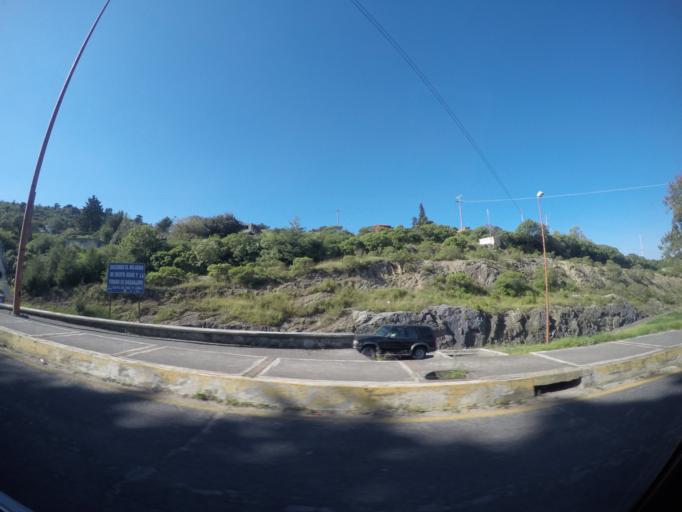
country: MX
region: Hidalgo
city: Mineral del Monte
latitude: 20.1393
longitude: -98.6865
